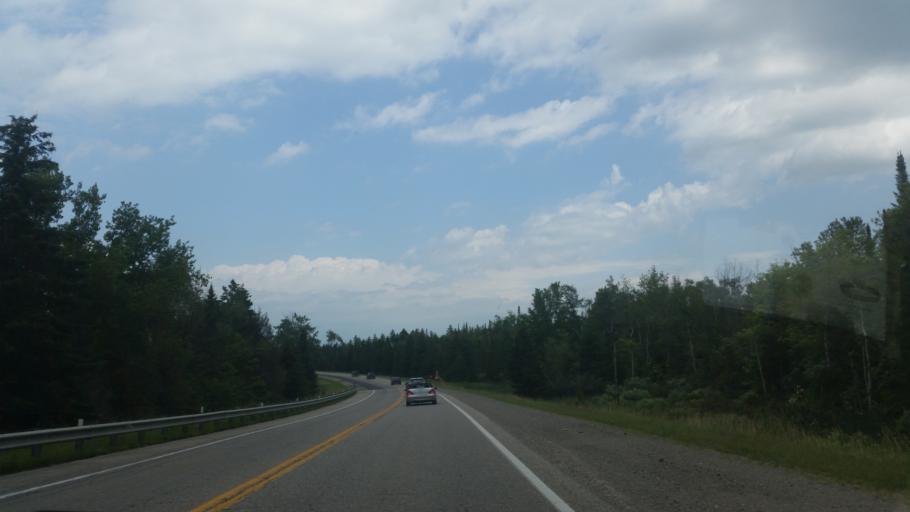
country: CA
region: Ontario
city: Orangeville
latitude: 43.7314
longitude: -80.0954
